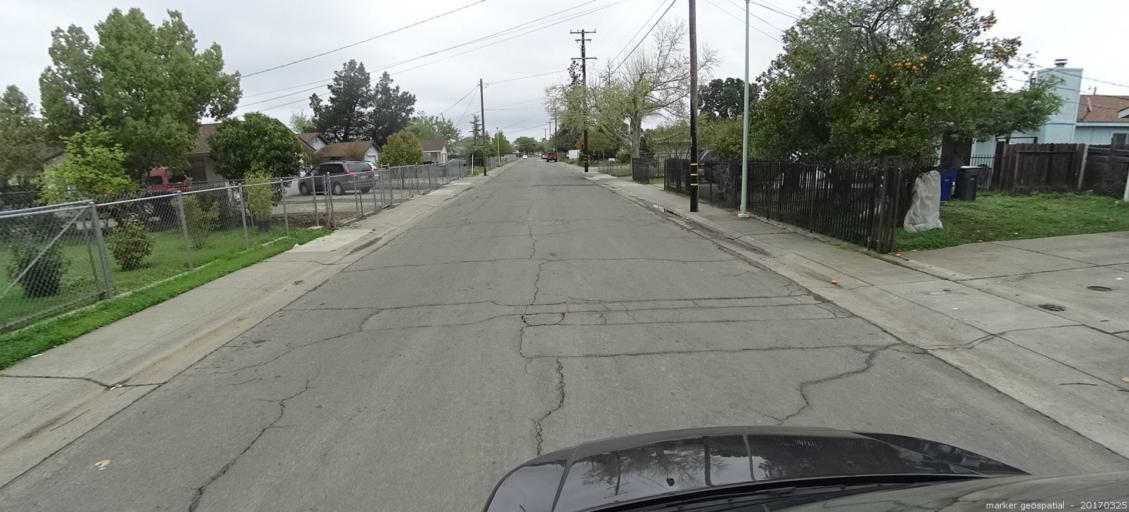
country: US
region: California
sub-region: Sacramento County
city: Florin
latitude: 38.5228
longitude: -121.4171
